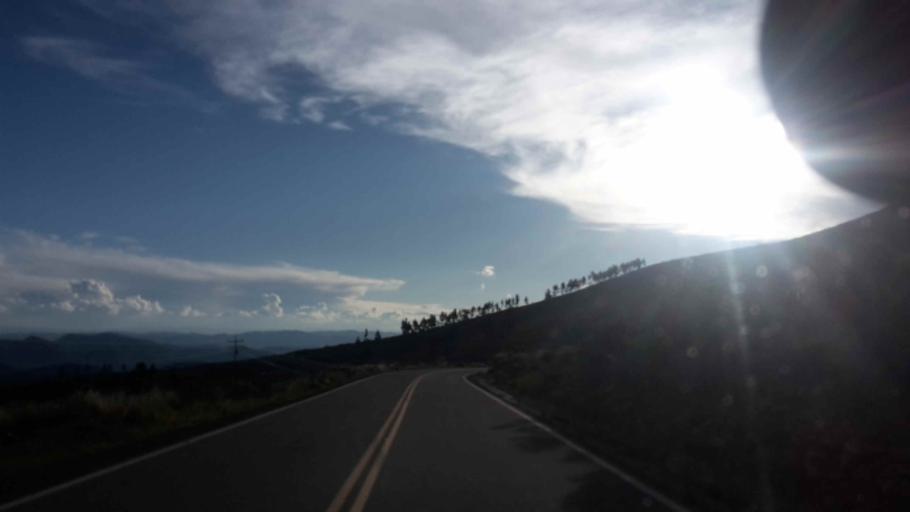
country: BO
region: Cochabamba
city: Arani
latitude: -17.5614
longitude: -65.7128
